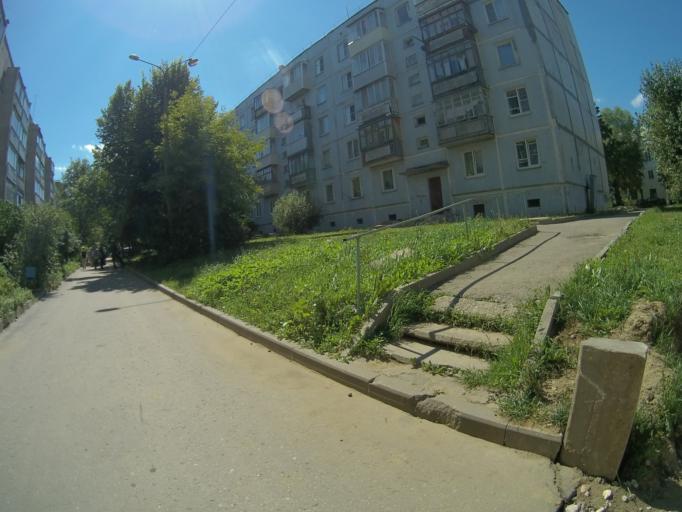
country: RU
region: Vladimir
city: Vladimir
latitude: 56.1333
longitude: 40.3721
